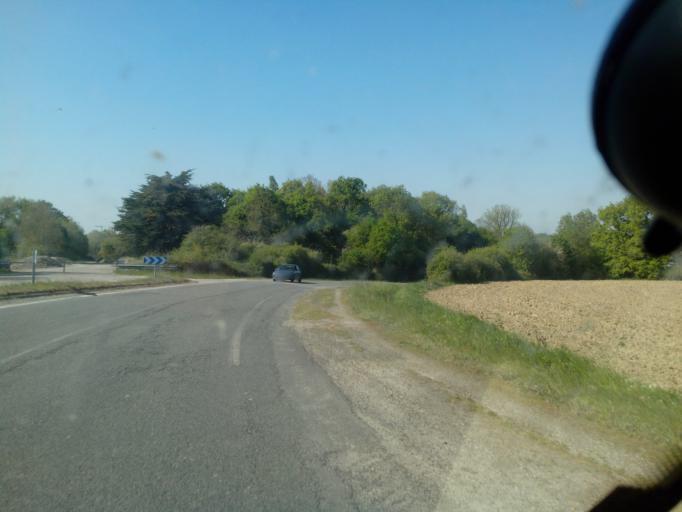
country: FR
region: Pays de la Loire
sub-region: Departement de la Loire-Atlantique
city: Pornic
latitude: 47.1089
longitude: -2.0749
